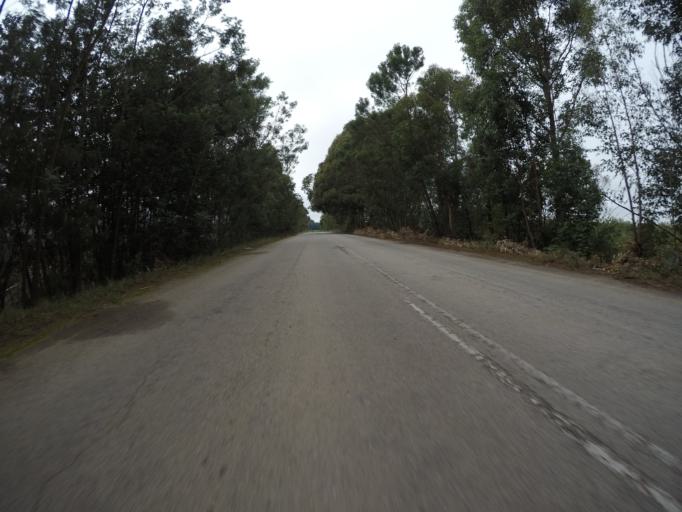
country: ZA
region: Eastern Cape
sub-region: Cacadu District Municipality
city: Kareedouw
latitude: -33.9982
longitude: 24.1707
